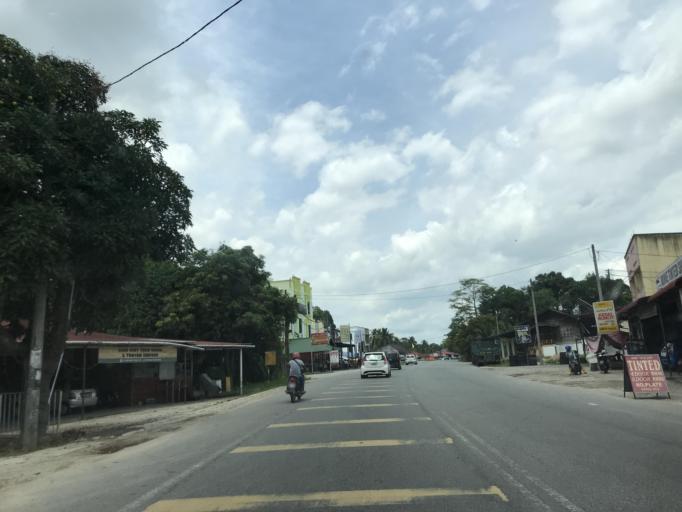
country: MY
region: Kelantan
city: Kota Bharu
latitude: 6.0776
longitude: 102.2085
